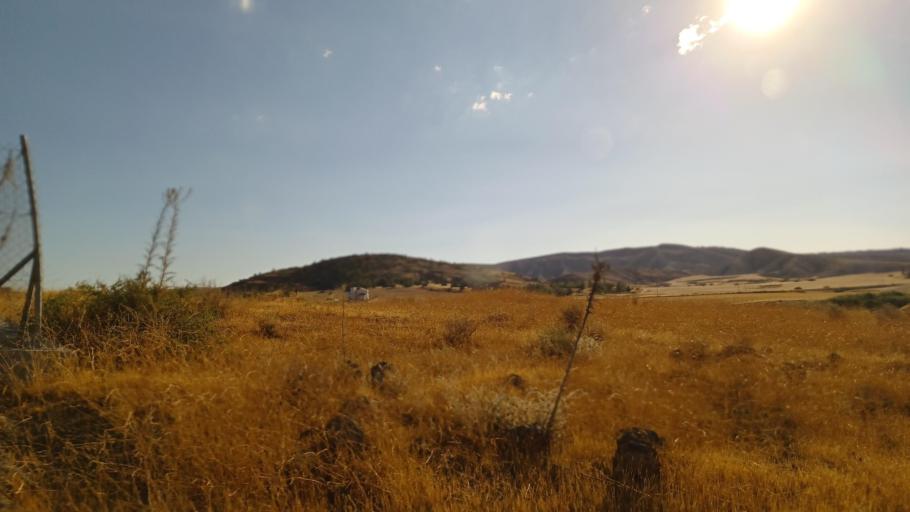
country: CY
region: Larnaka
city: Troulloi
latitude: 35.0114
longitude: 33.6359
